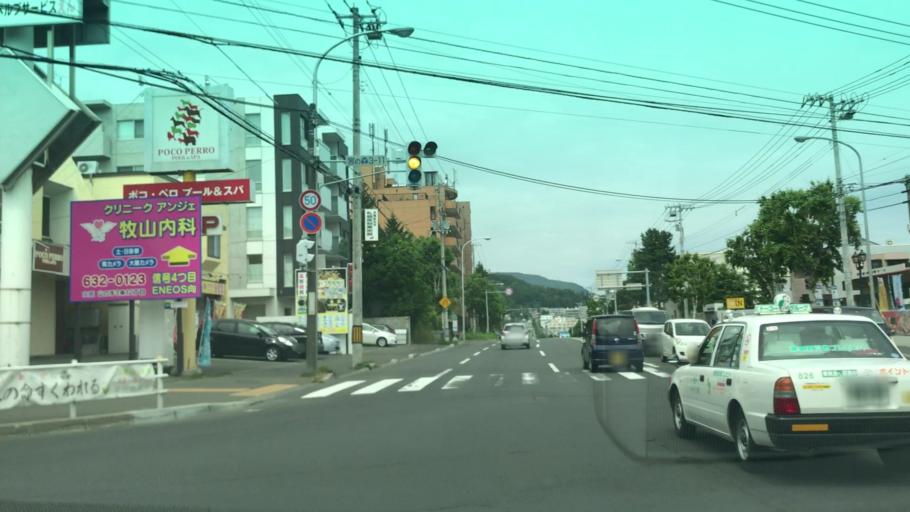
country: JP
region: Hokkaido
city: Sapporo
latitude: 43.0587
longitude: 141.3001
